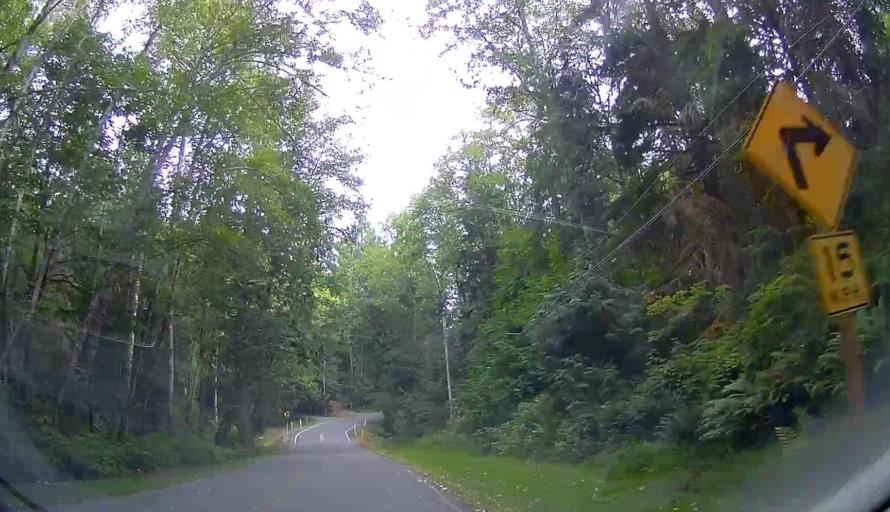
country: US
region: Washington
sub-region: Skagit County
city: Burlington
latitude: 48.5849
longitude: -122.3934
